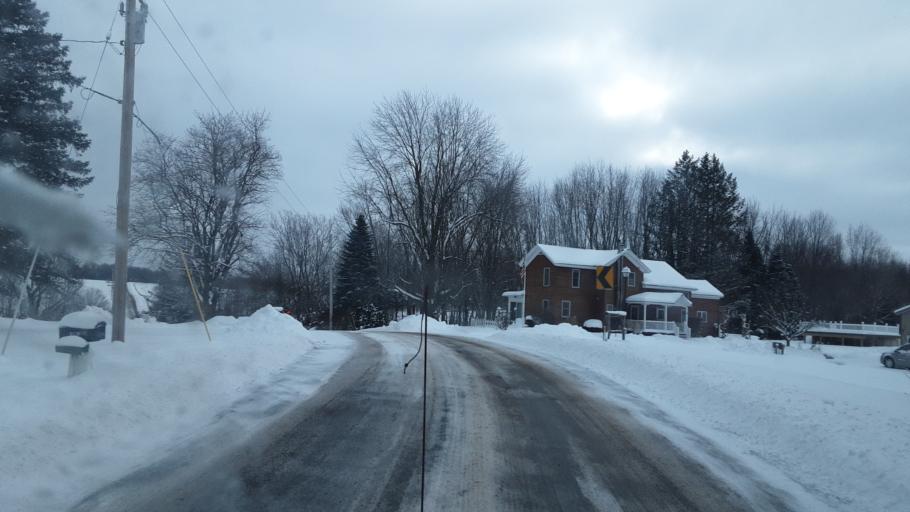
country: US
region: New York
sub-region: Wayne County
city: Lyons
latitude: 43.1381
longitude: -76.9946
